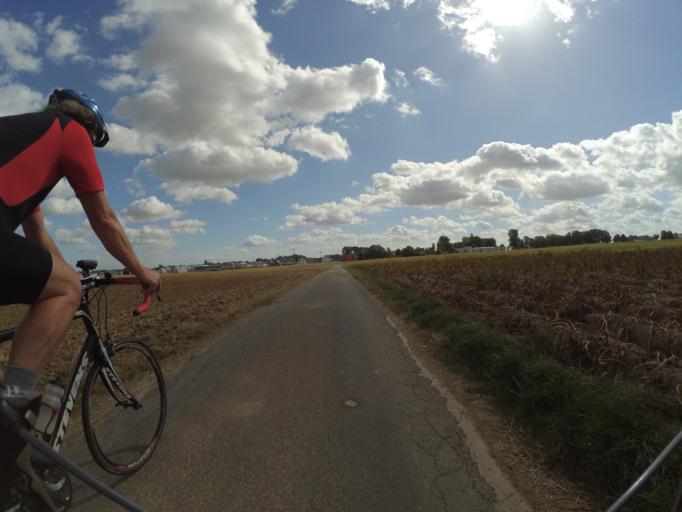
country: DE
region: North Rhine-Westphalia
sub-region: Regierungsbezirk Koln
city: Alsdorf
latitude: 50.8962
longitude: 6.1717
